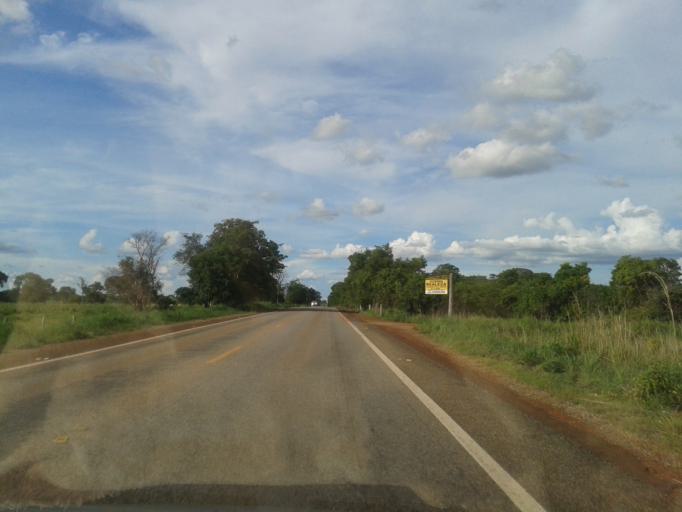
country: BR
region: Goias
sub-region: Mozarlandia
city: Mozarlandia
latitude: -14.2869
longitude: -50.4018
